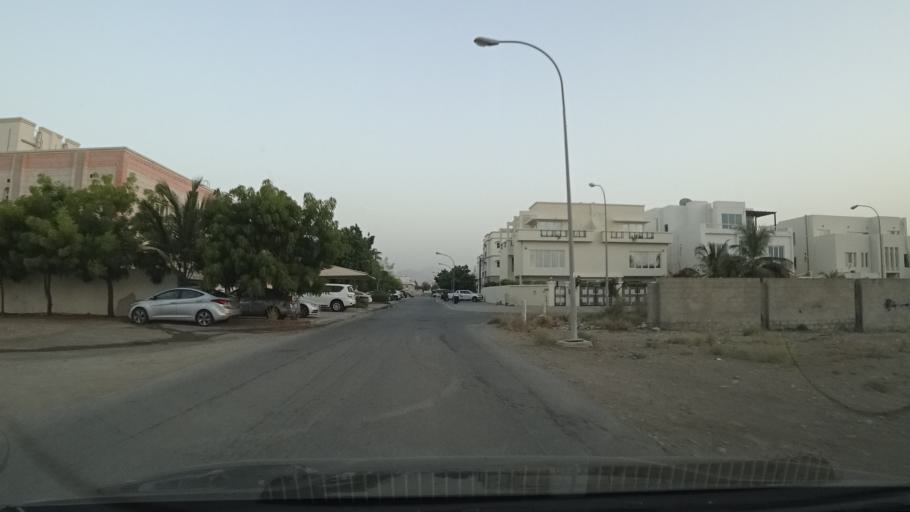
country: OM
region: Muhafazat Masqat
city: Bawshar
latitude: 23.6011
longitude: 58.3554
